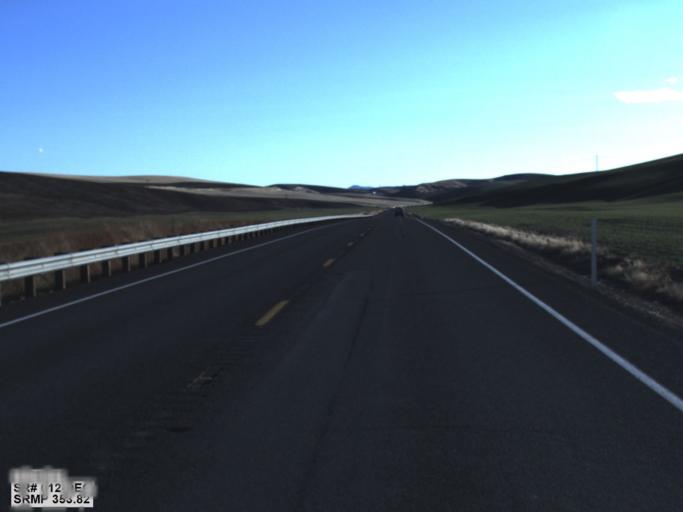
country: US
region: Washington
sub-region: Walla Walla County
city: Waitsburg
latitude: 46.2176
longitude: -118.1376
